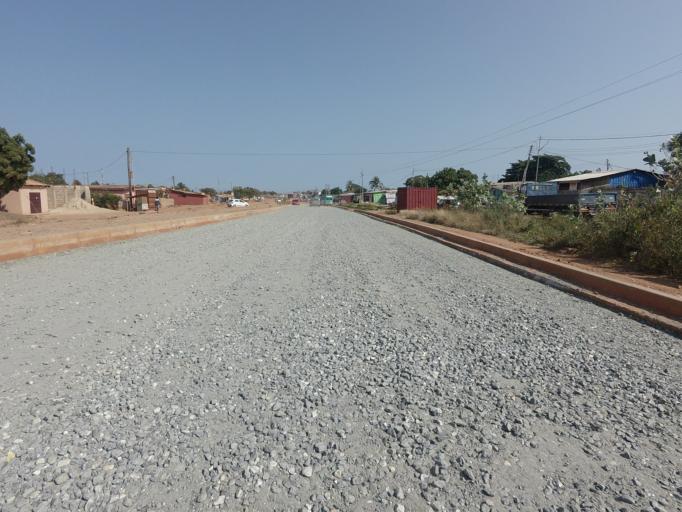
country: GH
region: Greater Accra
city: Teshi Old Town
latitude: 5.5903
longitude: -0.1160
